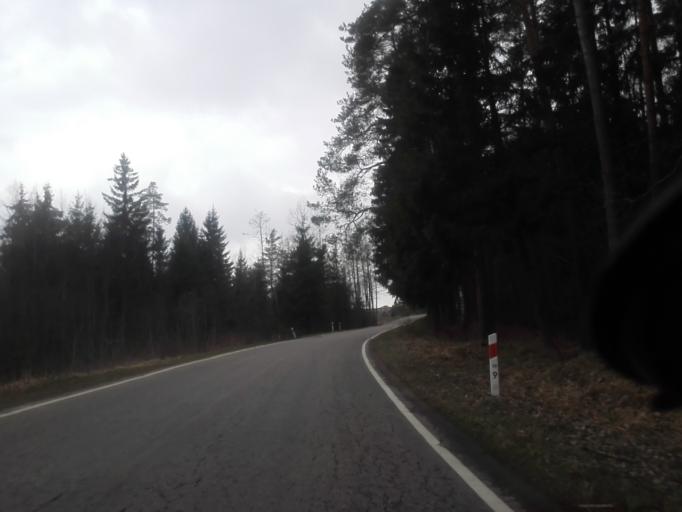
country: PL
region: Podlasie
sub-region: Powiat sejnenski
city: Krasnopol
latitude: 54.1646
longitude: 23.2257
